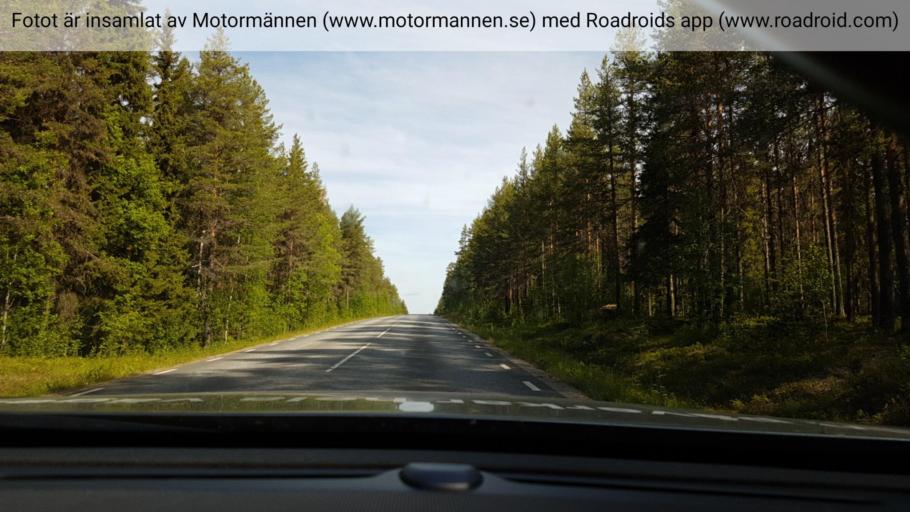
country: SE
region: Vaesterbotten
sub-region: Dorotea Kommun
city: Dorotea
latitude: 64.2709
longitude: 16.3467
